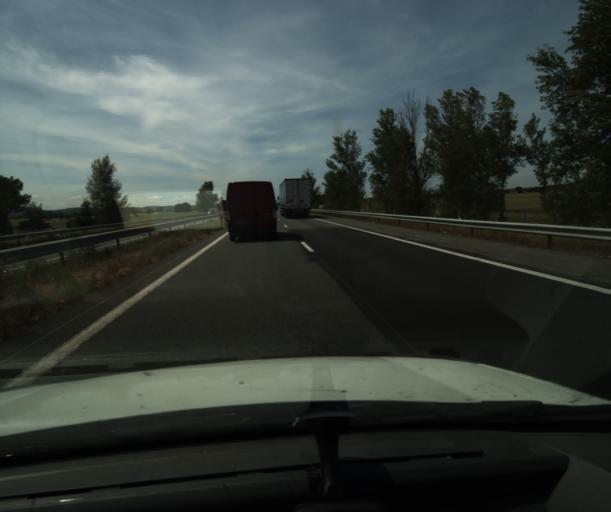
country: FR
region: Languedoc-Roussillon
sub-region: Departement de l'Aude
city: Saint-Martin-Lalande
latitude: 43.2576
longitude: 2.0324
